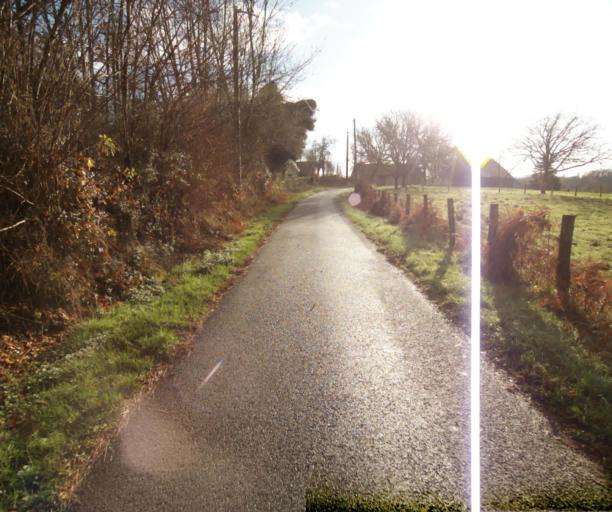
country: FR
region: Limousin
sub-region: Departement de la Correze
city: Sainte-Fereole
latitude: 45.2609
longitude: 1.6022
